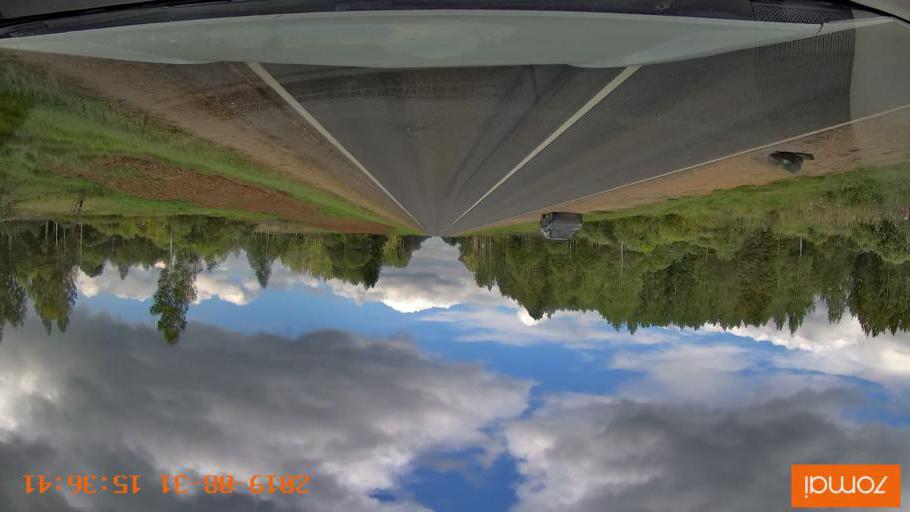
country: RU
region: Kaluga
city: Mosal'sk
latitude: 54.6129
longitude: 34.7650
